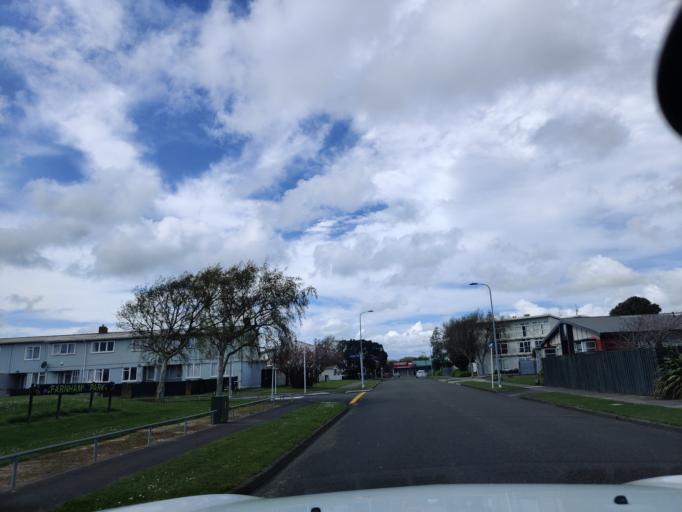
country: NZ
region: Manawatu-Wanganui
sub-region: Palmerston North City
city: Palmerston North
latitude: -40.3576
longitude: 175.5875
